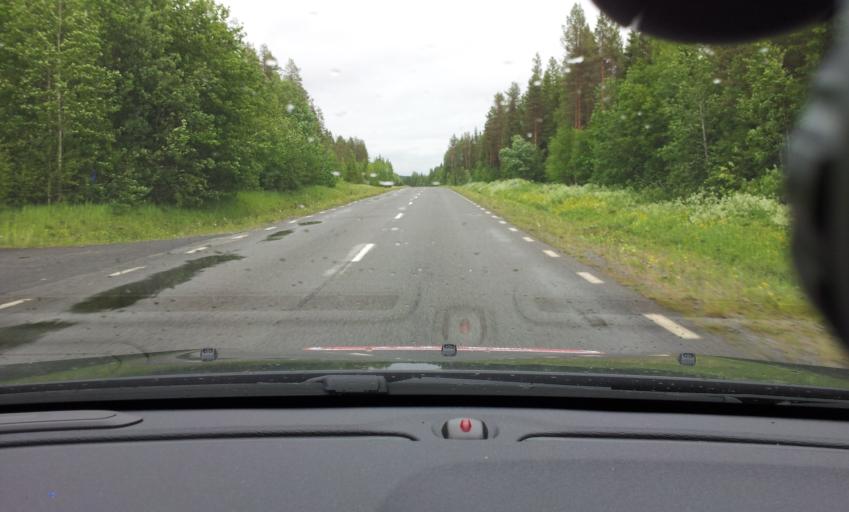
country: SE
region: Jaemtland
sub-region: OEstersunds Kommun
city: Lit
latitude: 63.7331
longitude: 14.9009
